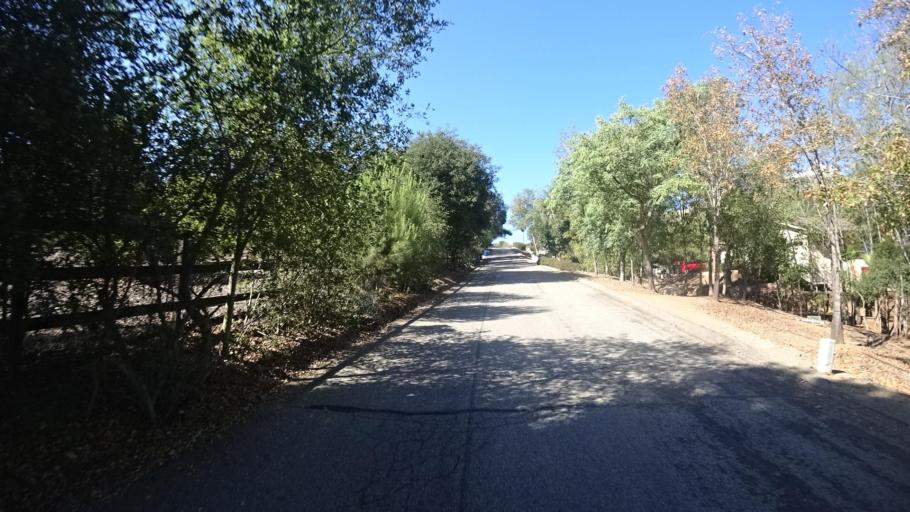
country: US
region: California
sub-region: San Diego County
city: Hidden Meadows
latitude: 33.2314
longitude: -117.1194
